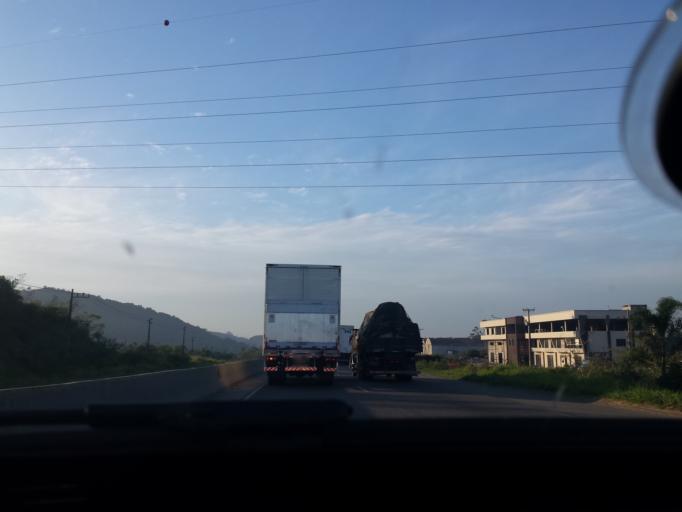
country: BR
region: Santa Catarina
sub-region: Imbituba
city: Imbituba
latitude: -28.2233
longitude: -48.7009
